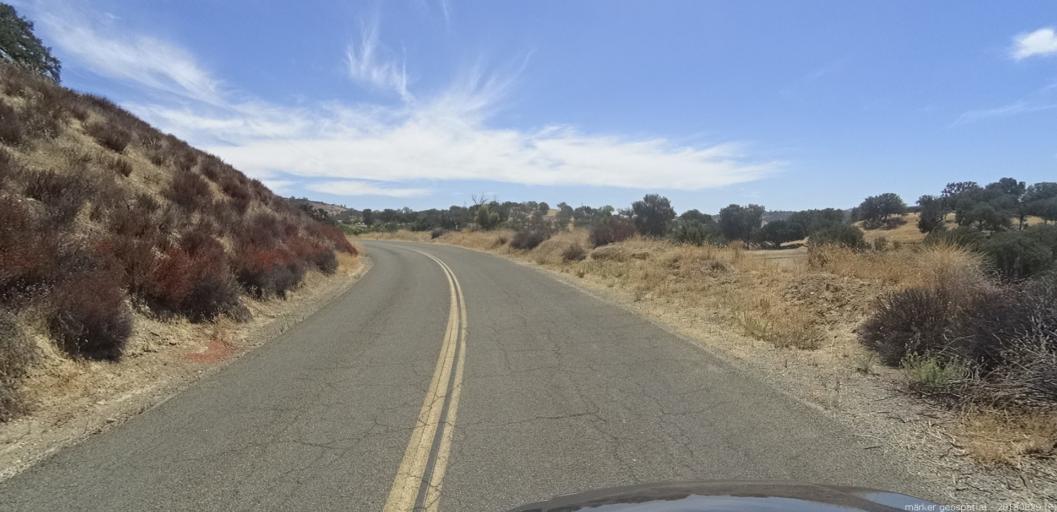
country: US
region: California
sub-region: San Luis Obispo County
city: Lake Nacimiento
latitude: 35.8614
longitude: -120.9675
